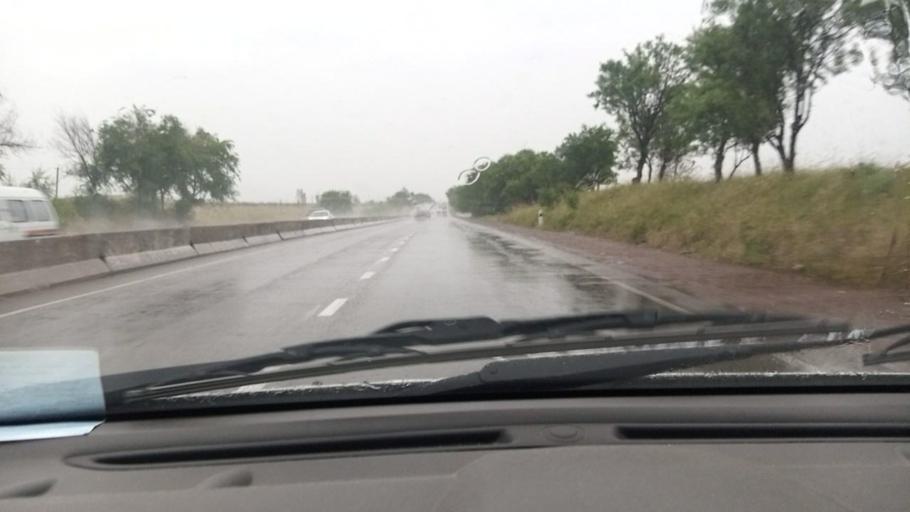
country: UZ
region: Toshkent
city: Angren
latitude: 40.9539
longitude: 69.9248
